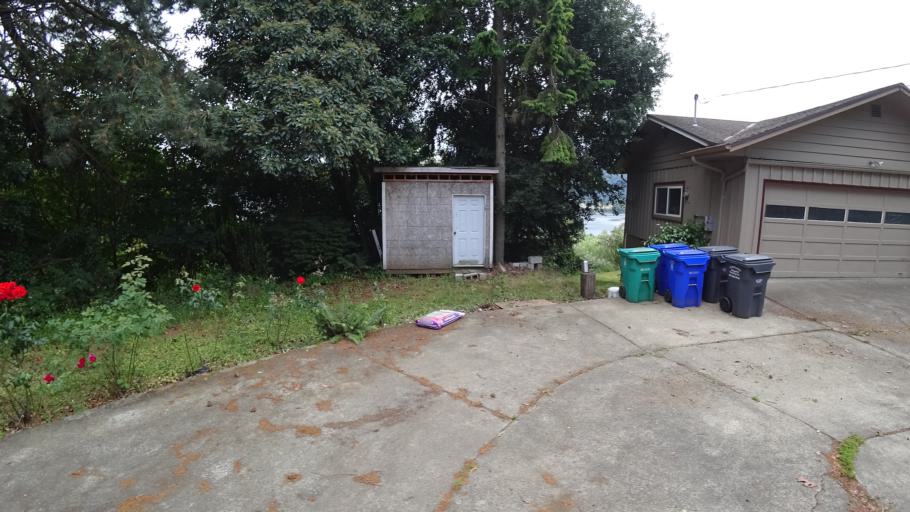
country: US
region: Oregon
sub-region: Washington County
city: West Haven
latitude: 45.5775
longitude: -122.7341
